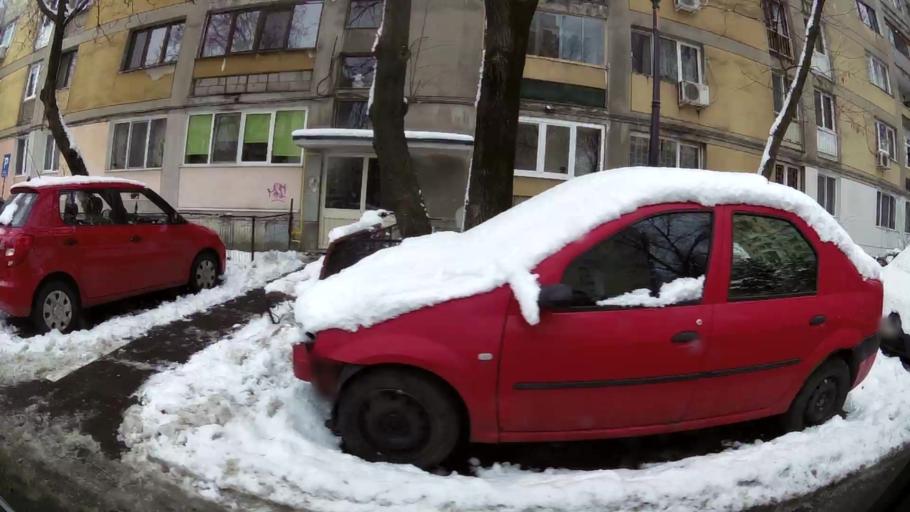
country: RO
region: Bucuresti
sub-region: Municipiul Bucuresti
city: Bucuresti
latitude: 44.3889
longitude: 26.1152
